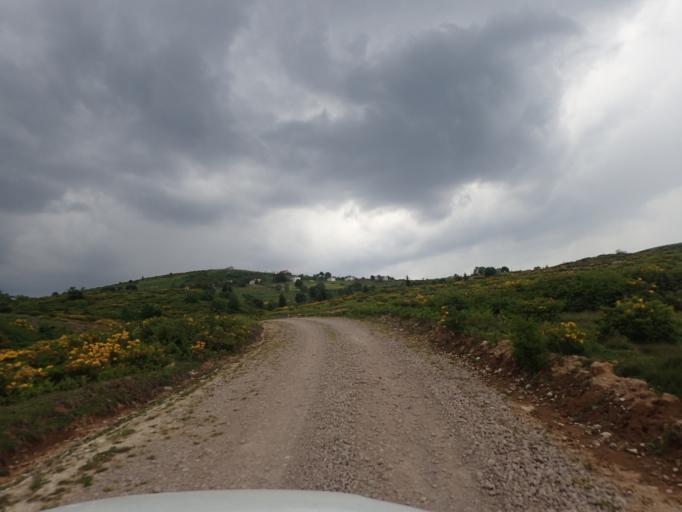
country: TR
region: Ordu
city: Topcam
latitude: 40.6761
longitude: 37.9253
